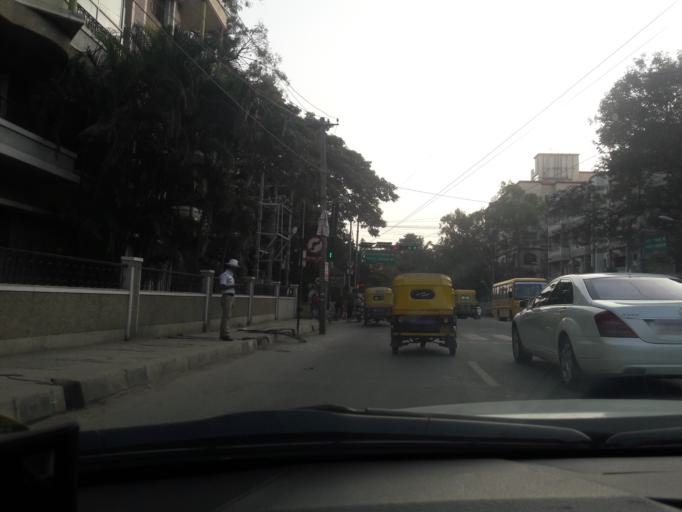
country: IN
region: Karnataka
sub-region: Bangalore Urban
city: Bangalore
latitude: 13.0043
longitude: 77.6198
